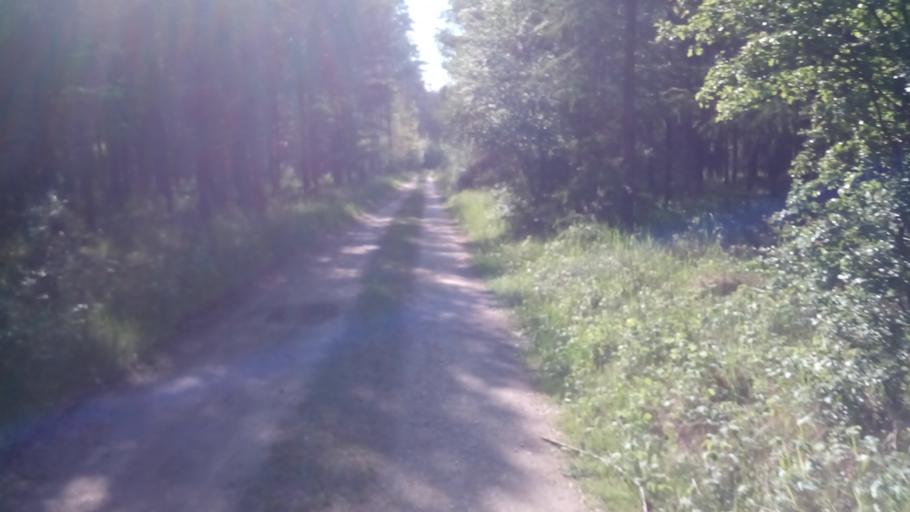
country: PL
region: Opole Voivodeship
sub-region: Powiat opolski
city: Tarnow Opolski
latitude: 50.5846
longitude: 18.0613
